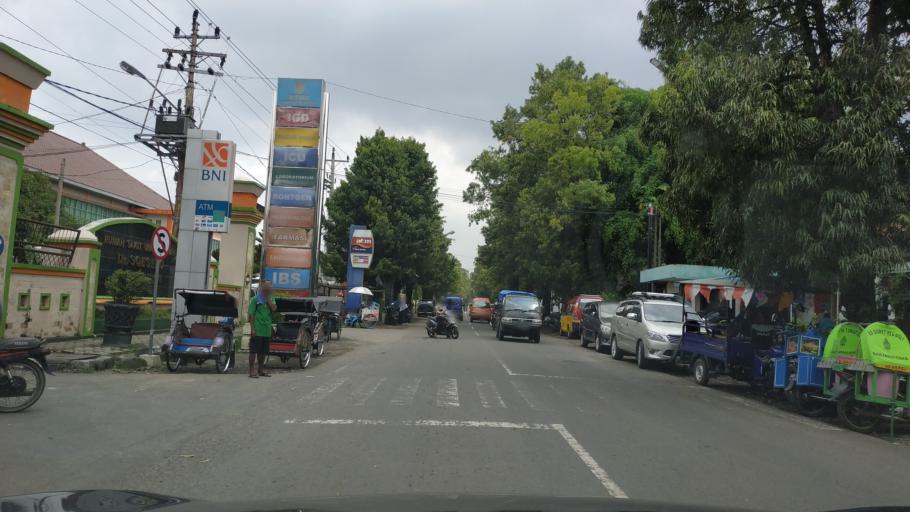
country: ID
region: Central Java
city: Slawi
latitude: -6.9931
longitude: 109.1378
